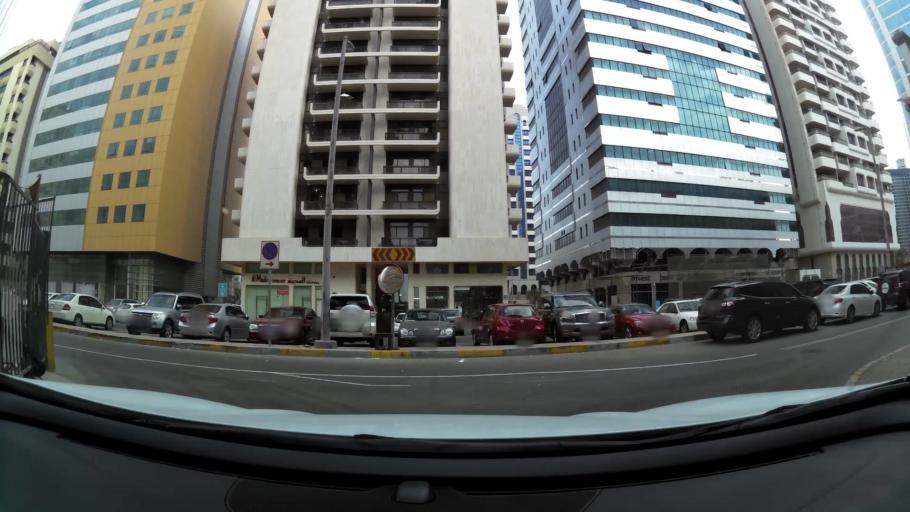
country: AE
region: Abu Dhabi
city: Abu Dhabi
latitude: 24.4871
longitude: 54.3524
